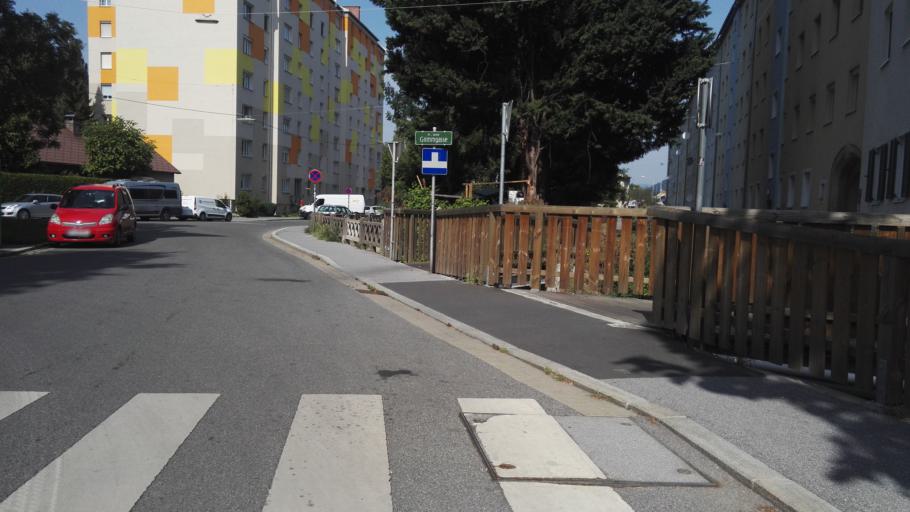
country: AT
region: Styria
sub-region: Graz Stadt
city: Goesting
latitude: 47.0850
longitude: 15.4222
